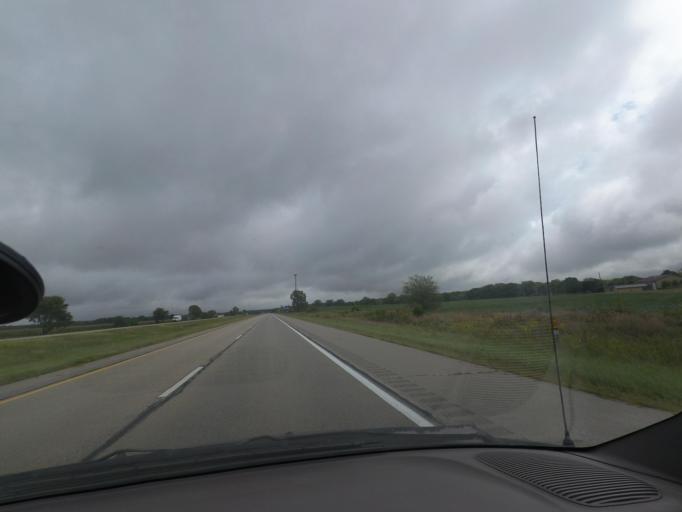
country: US
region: Illinois
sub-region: Piatt County
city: Monticello
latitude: 40.0397
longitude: -88.5900
